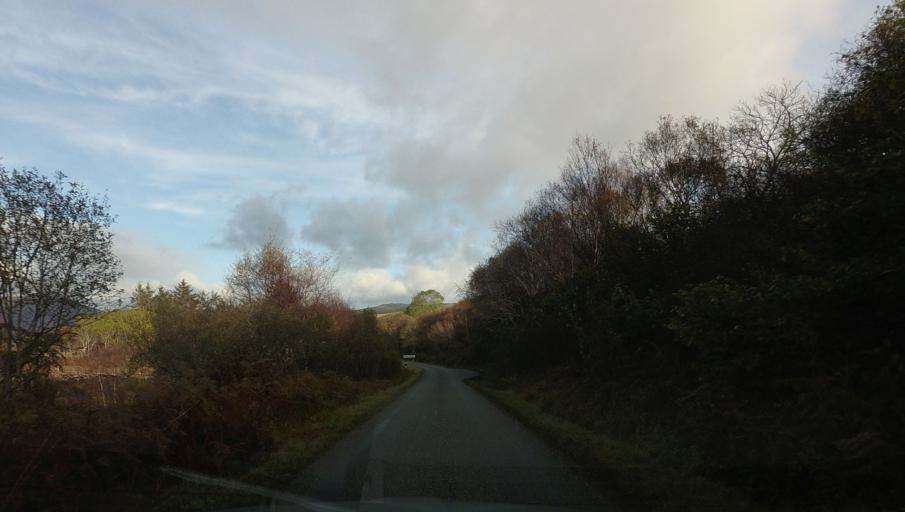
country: GB
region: Scotland
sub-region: Argyll and Bute
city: Isle Of Mull
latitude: 56.3598
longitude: -6.0450
